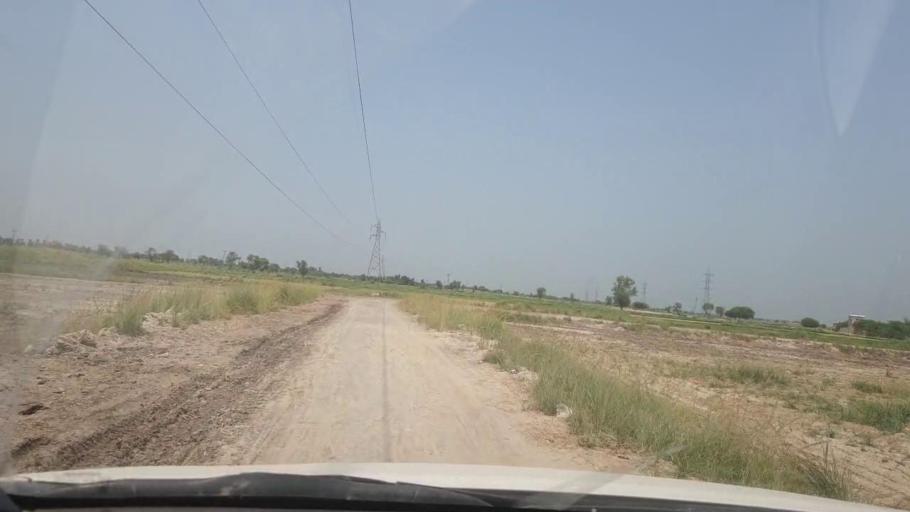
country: PK
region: Sindh
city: Lakhi
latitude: 27.8640
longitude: 68.6973
